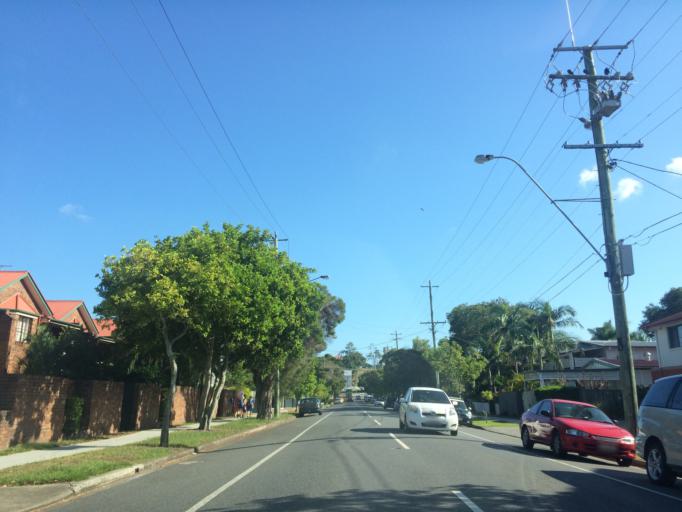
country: AU
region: Queensland
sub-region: Brisbane
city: Balmoral
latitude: -27.4547
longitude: 153.0617
